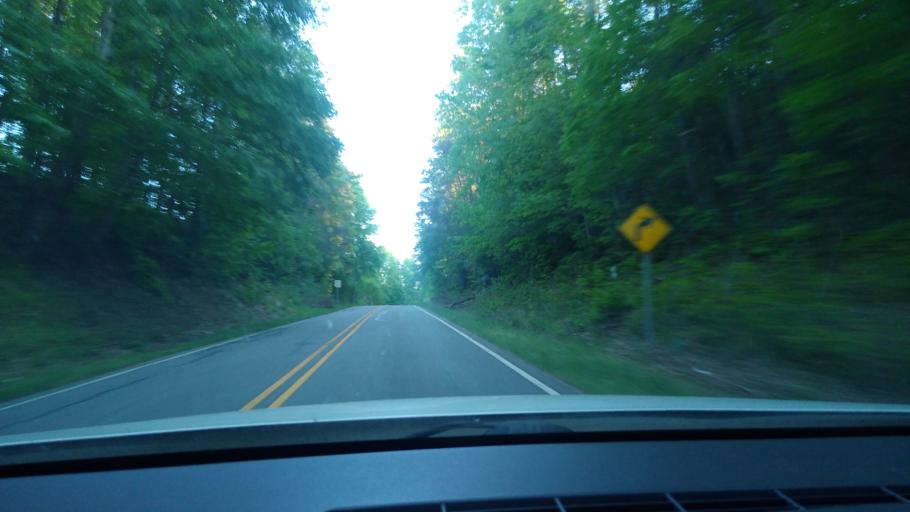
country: US
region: North Carolina
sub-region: Rockingham County
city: Reidsville
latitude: 36.3722
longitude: -79.5515
